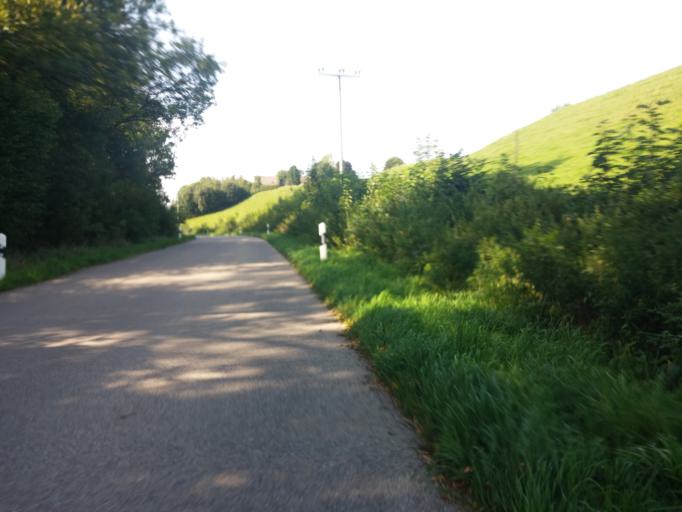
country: DE
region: Bavaria
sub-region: Swabia
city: Lautrach
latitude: 47.9171
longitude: 10.1251
